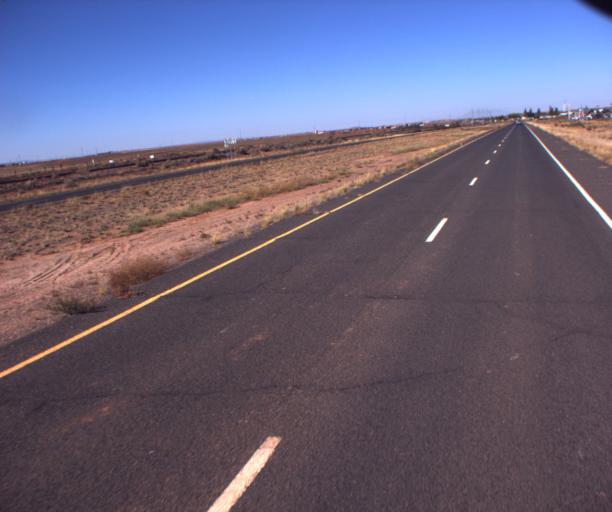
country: US
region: Arizona
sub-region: Navajo County
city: Winslow
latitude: 35.0115
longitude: -110.6697
